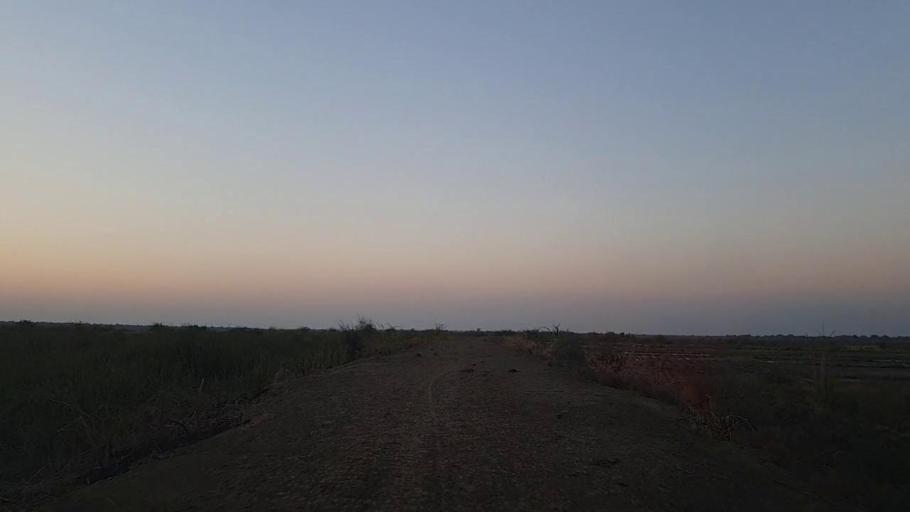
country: PK
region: Sindh
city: Tando Mittha Khan
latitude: 26.0721
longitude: 69.1560
